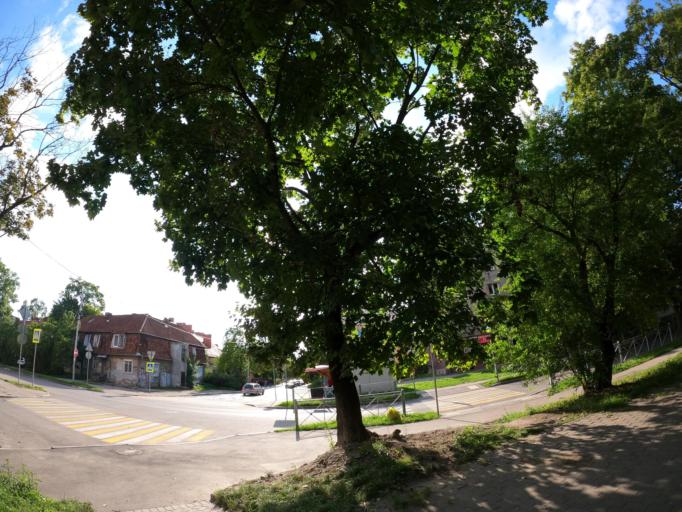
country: RU
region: Kaliningrad
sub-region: Gorod Kaliningrad
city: Kaliningrad
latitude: 54.7256
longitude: 20.4645
